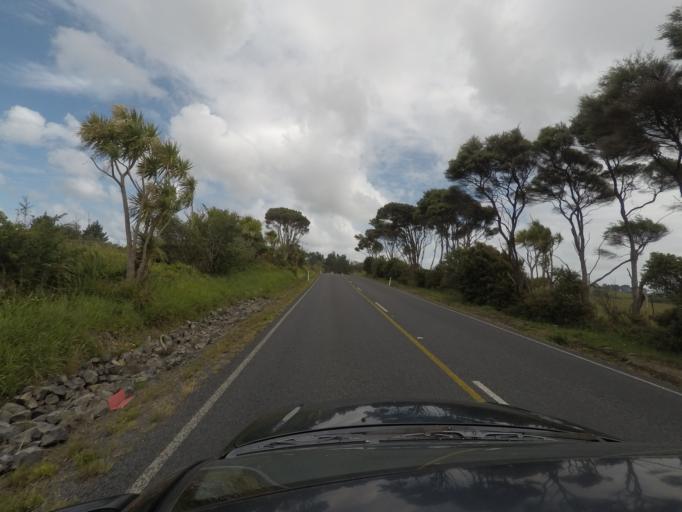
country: NZ
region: Auckland
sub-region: Auckland
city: Parakai
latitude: -36.6338
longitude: 174.5046
